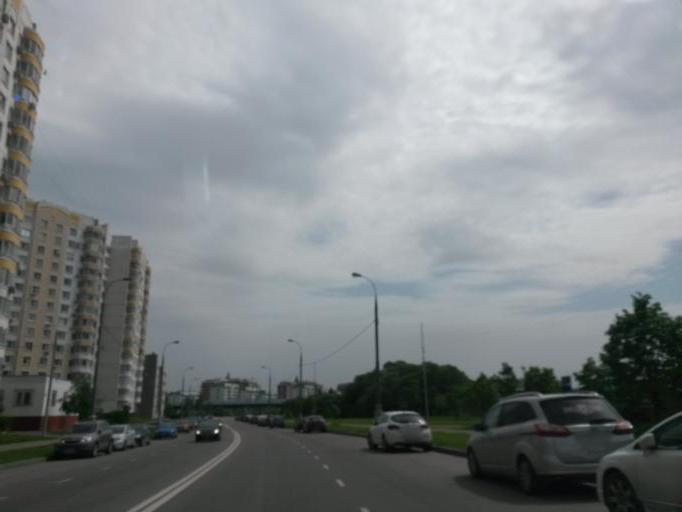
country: RU
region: Moskovskaya
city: Kommunarka
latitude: 55.5447
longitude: 37.5285
